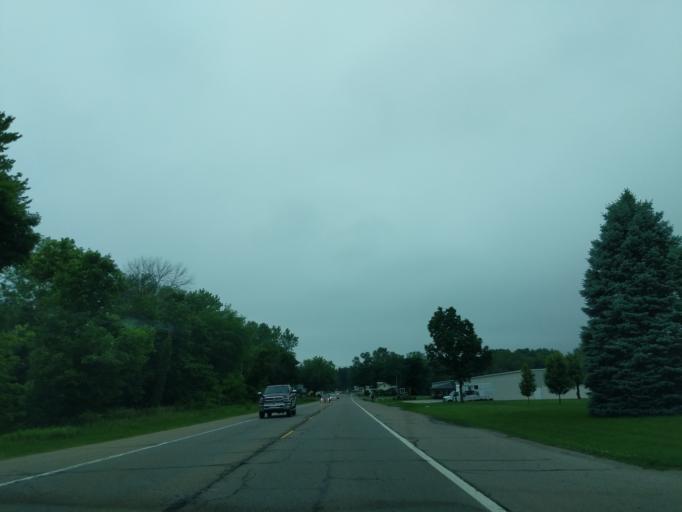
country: US
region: Michigan
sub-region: Branch County
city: Quincy
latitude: 41.9401
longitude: -84.9358
